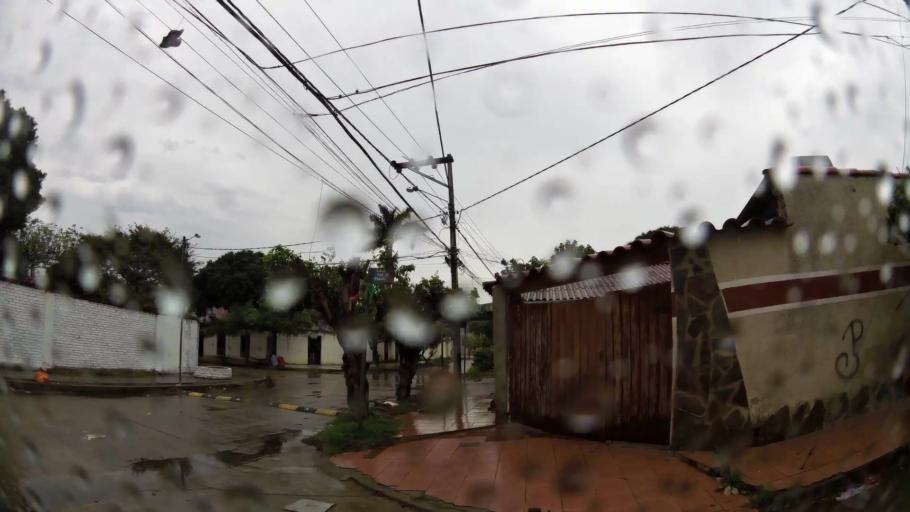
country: BO
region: Santa Cruz
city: Santa Cruz de la Sierra
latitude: -17.7844
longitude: -63.1551
